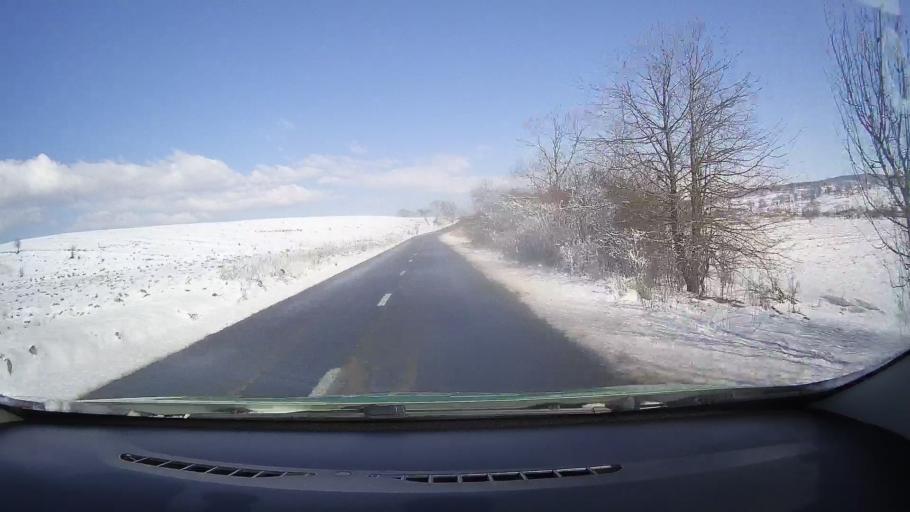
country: RO
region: Sibiu
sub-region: Comuna Rosia
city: Rosia
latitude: 45.8505
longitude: 24.3081
